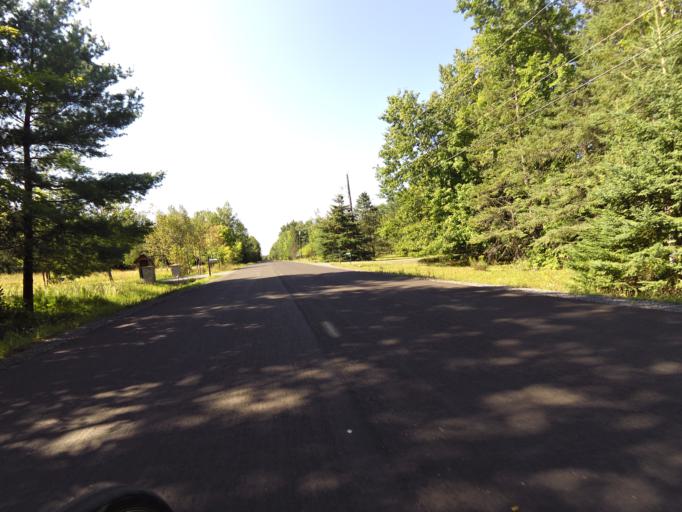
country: CA
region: Ontario
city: Bells Corners
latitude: 45.4604
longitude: -75.9752
